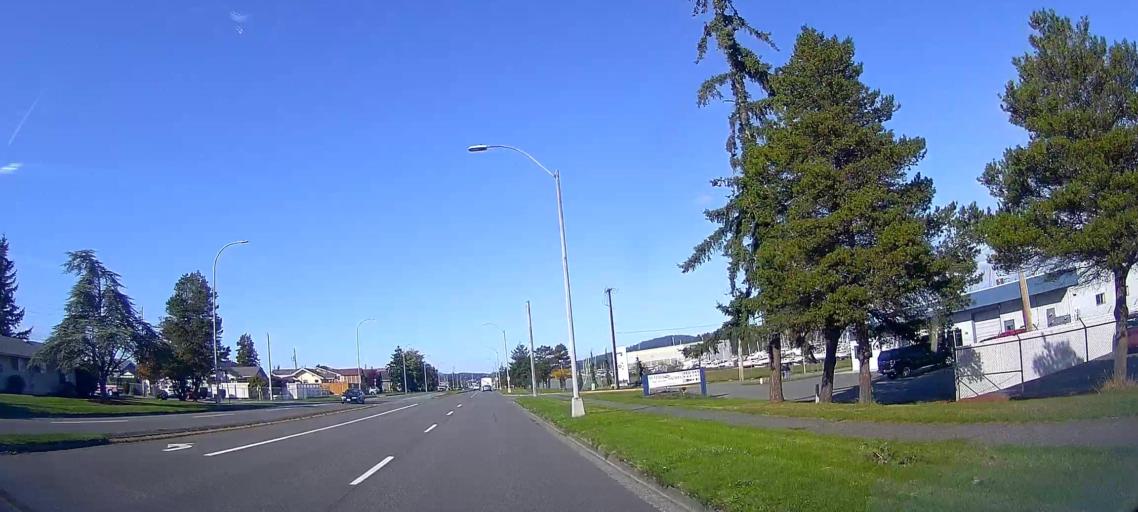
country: US
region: Washington
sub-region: Skagit County
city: Anacortes
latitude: 48.4991
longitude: -122.6095
